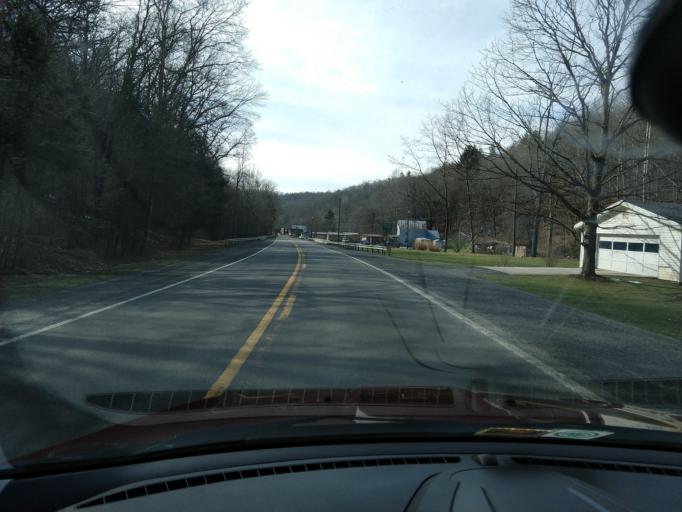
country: US
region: West Virginia
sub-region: Pocahontas County
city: Marlinton
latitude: 38.1956
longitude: -80.1357
